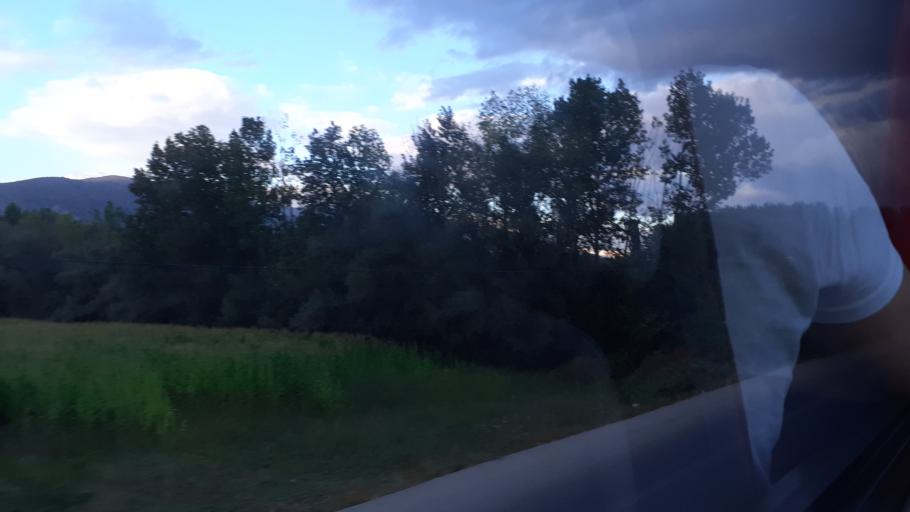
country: TR
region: Tokat
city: Dokmetepe
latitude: 40.3223
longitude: 36.2246
